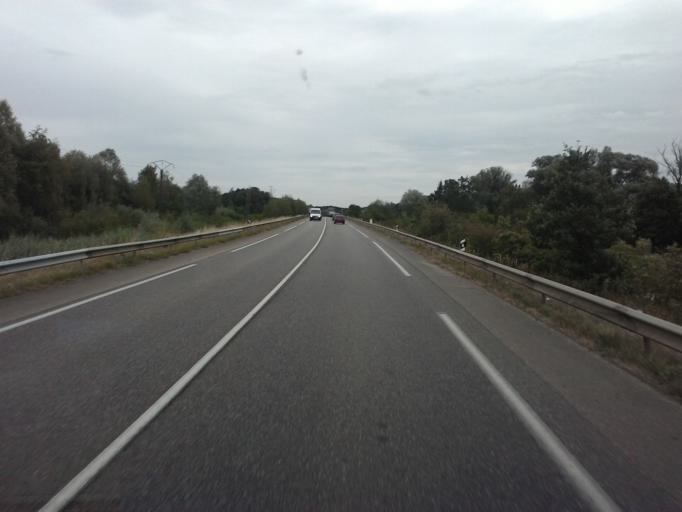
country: FR
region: Lorraine
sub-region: Departement de Meurthe-et-Moselle
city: Messein
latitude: 48.5987
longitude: 6.1360
